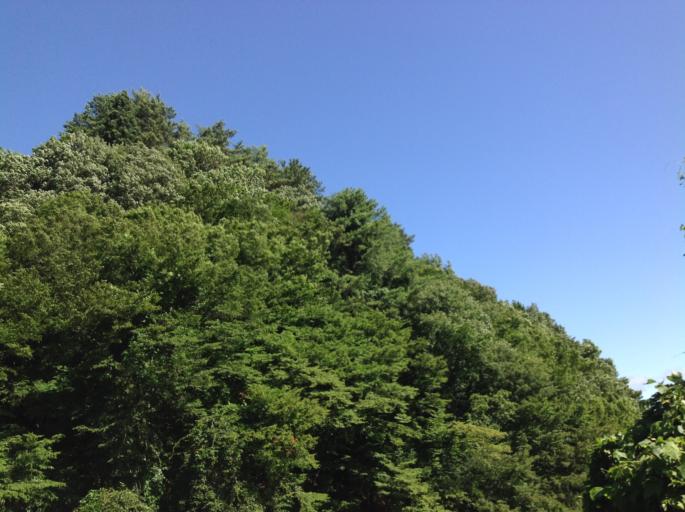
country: JP
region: Akita
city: Kakunodatemachi
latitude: 39.7009
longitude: 140.6756
